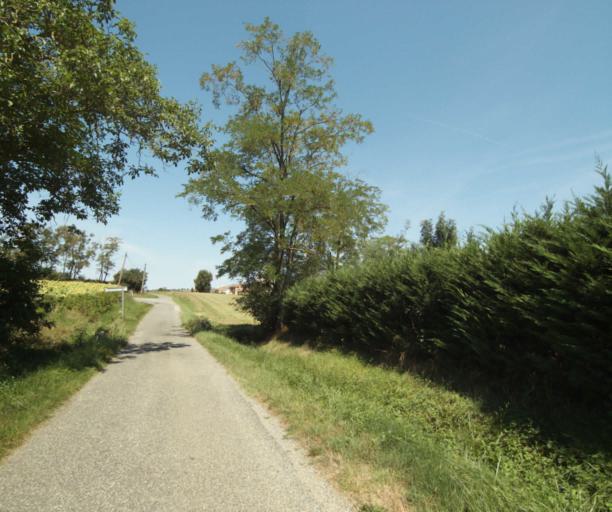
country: FR
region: Midi-Pyrenees
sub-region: Departement de l'Ariege
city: Lezat-sur-Leze
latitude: 43.2826
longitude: 1.3438
